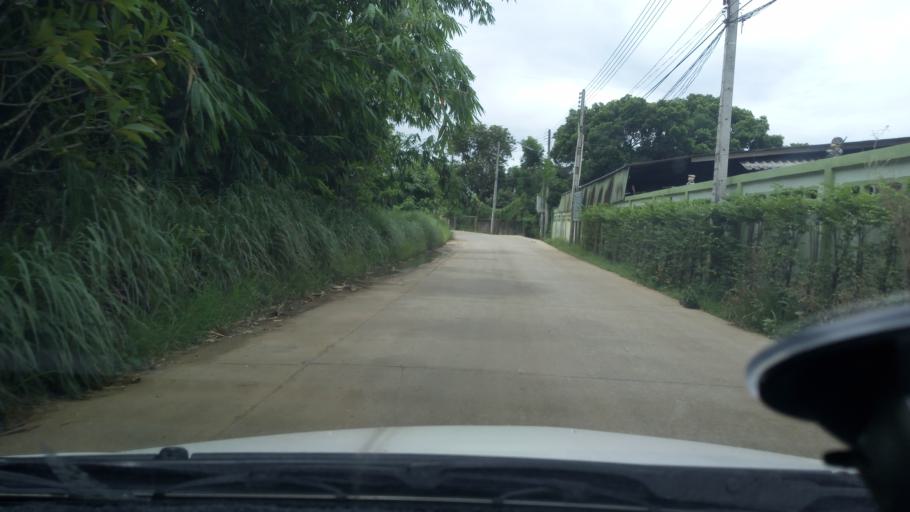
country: TH
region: Chon Buri
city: Phanat Nikhom
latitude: 13.4971
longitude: 101.1665
